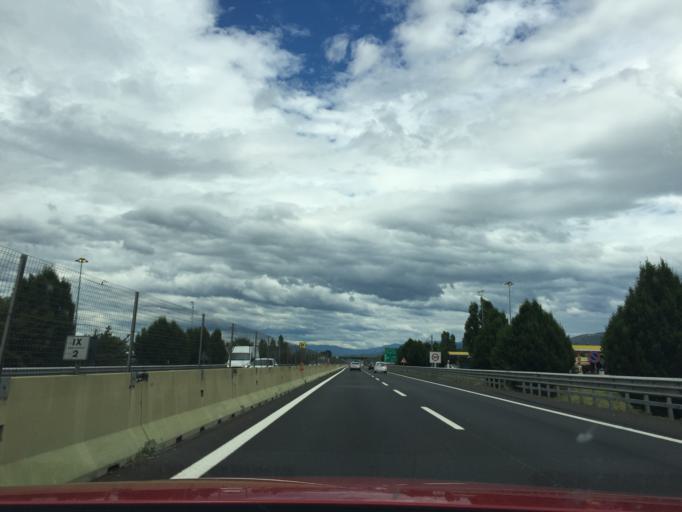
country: IT
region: Tuscany
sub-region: Province of Florence
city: Sesto Fiorentino
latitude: 43.8177
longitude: 11.1751
